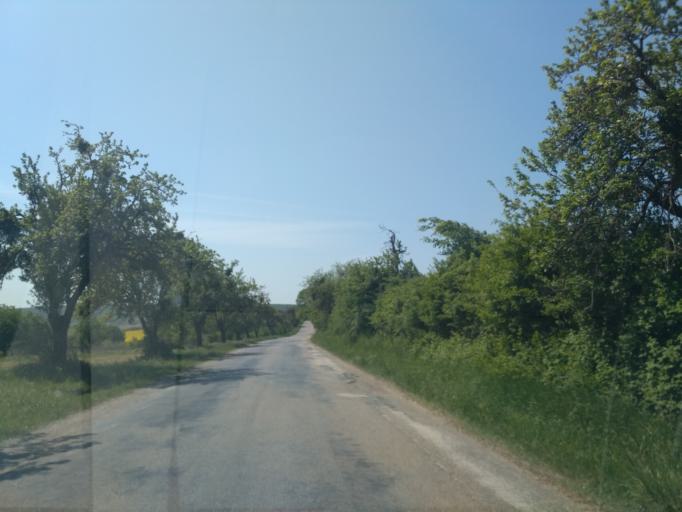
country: SK
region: Kosicky
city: Kosice
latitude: 48.7859
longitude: 21.3392
